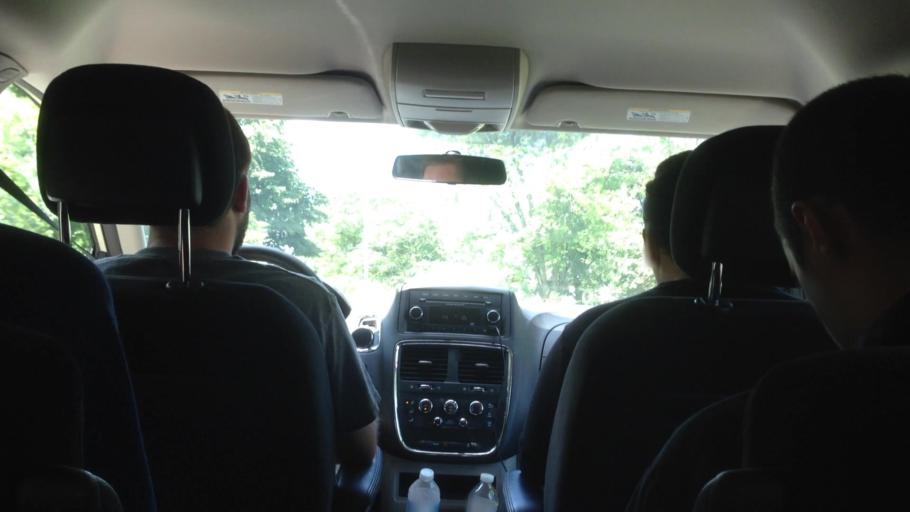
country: US
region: New York
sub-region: Dutchess County
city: Tivoli
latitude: 42.0505
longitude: -73.8736
